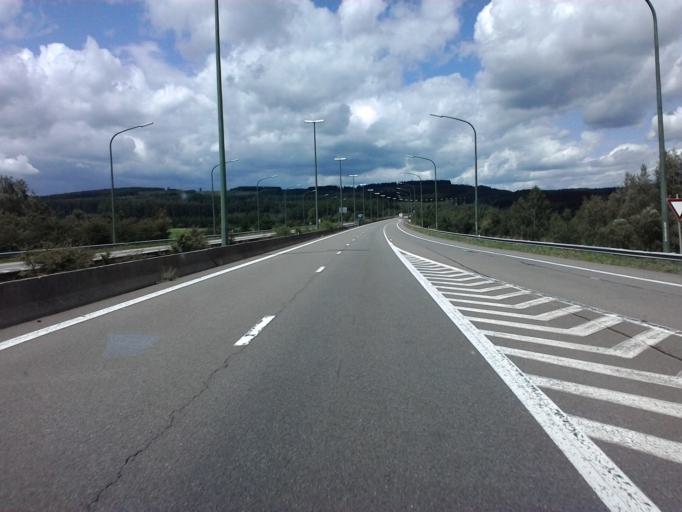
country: BE
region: Wallonia
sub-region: Province du Luxembourg
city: Manhay
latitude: 50.3097
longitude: 5.7125
